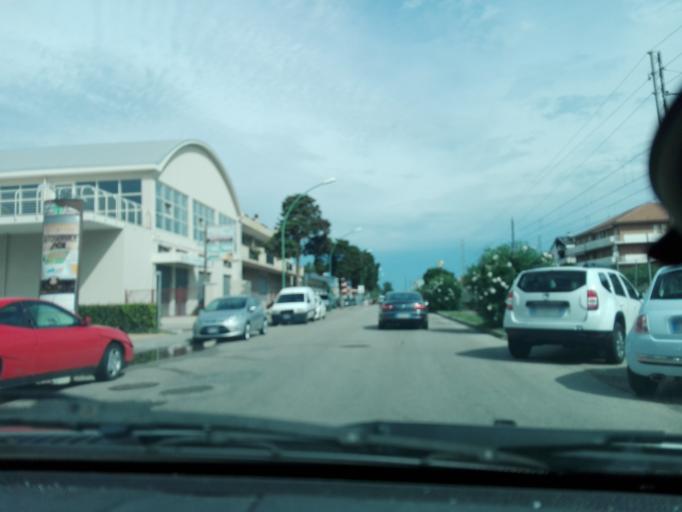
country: IT
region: Abruzzo
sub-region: Provincia di Teramo
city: Pineto
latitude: 42.6150
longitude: 14.0621
